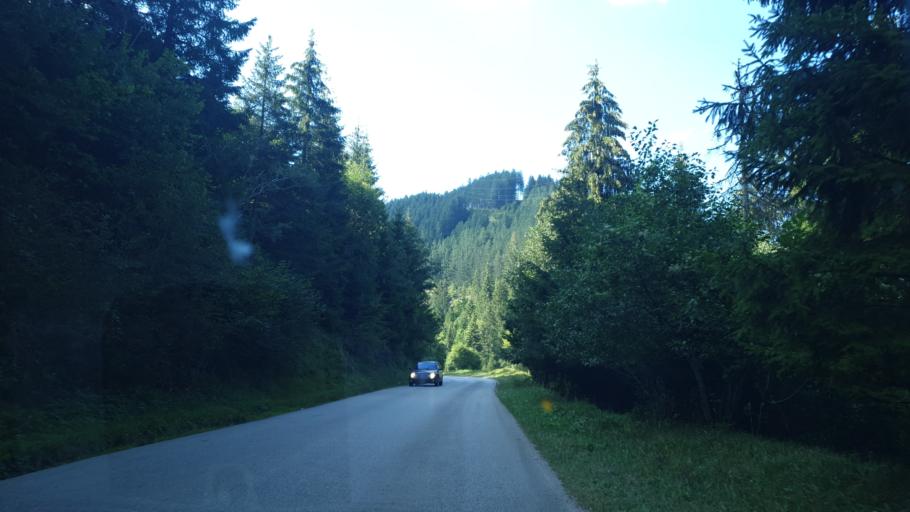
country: RS
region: Central Serbia
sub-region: Zlatiborski Okrug
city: Nova Varos
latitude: 43.4568
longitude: 19.8388
